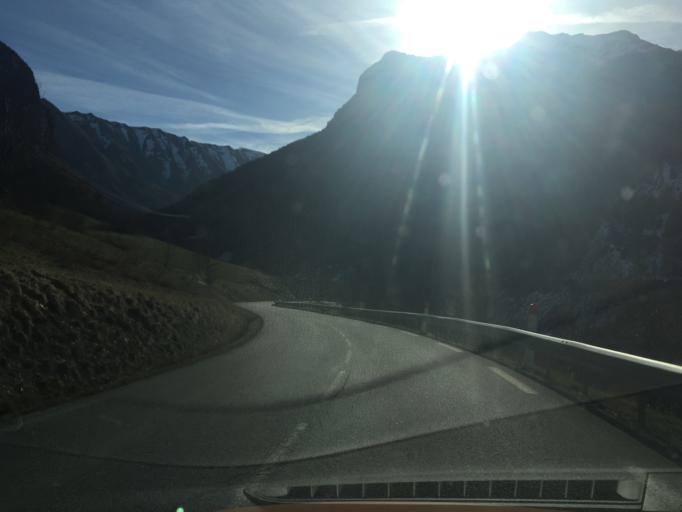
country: FR
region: Provence-Alpes-Cote d'Azur
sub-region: Departement des Hautes-Alpes
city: Embrun
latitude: 44.5126
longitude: 6.5623
